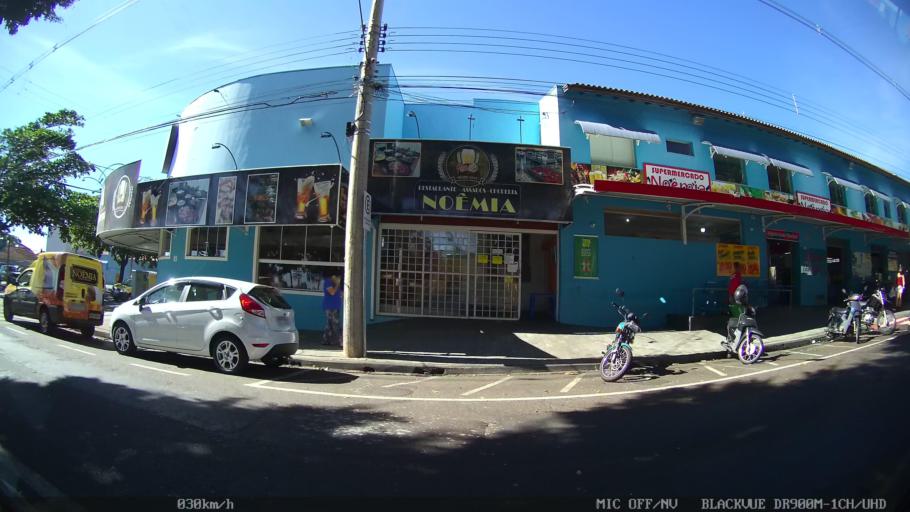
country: BR
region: Sao Paulo
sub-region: Franca
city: Franca
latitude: -20.5579
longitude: -47.3727
